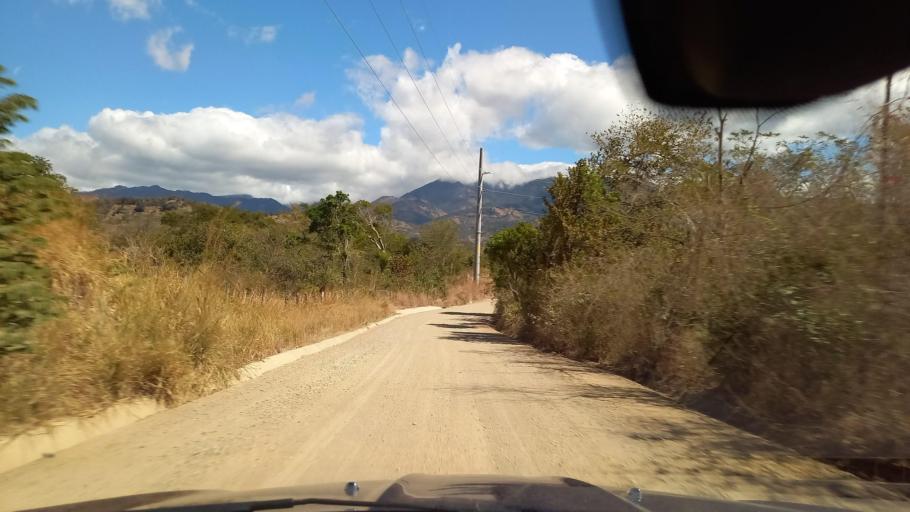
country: SV
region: Santa Ana
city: Metapan
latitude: 14.3602
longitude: -89.4759
